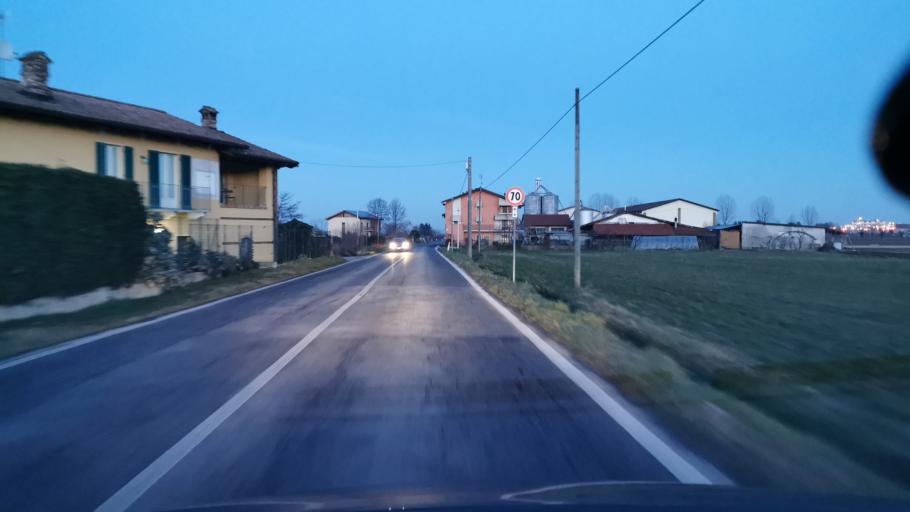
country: IT
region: Piedmont
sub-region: Provincia di Cuneo
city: Roata Rossi
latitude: 44.4408
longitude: 7.5522
